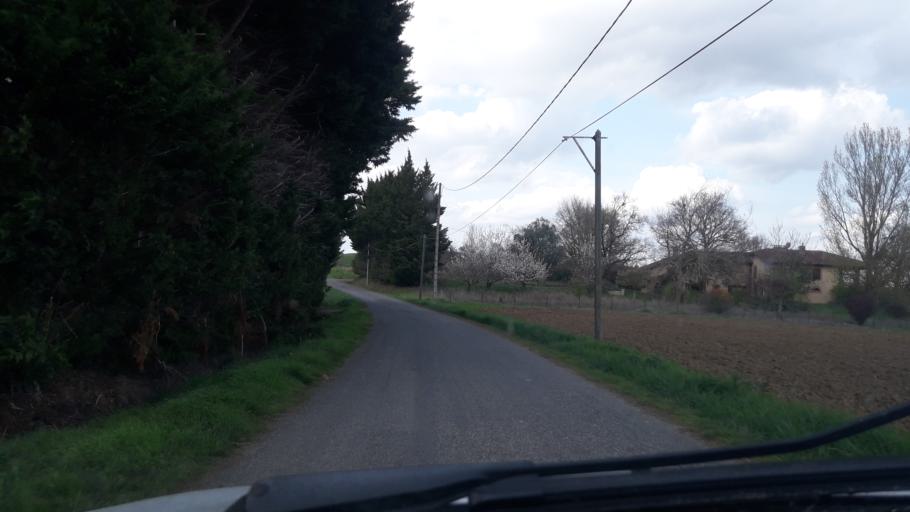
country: FR
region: Midi-Pyrenees
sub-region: Departement de la Haute-Garonne
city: Montesquieu-Volvestre
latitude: 43.2103
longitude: 1.3065
